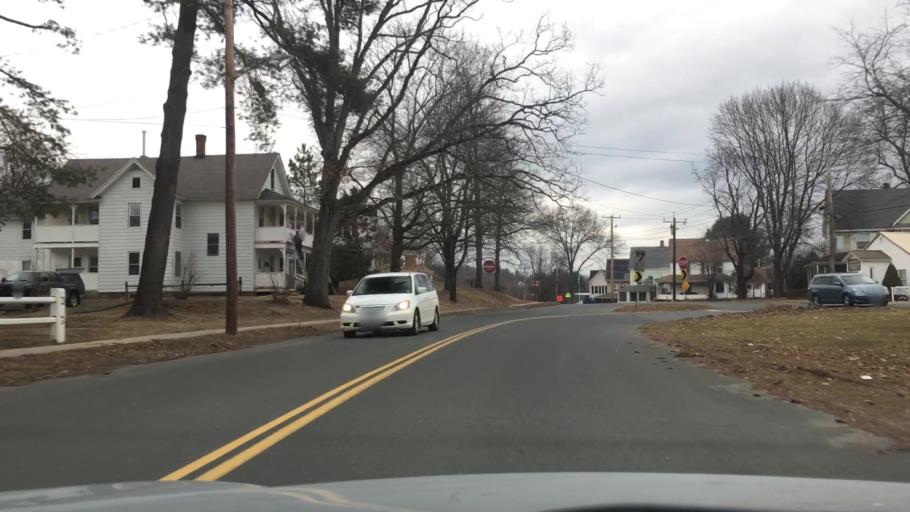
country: US
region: Massachusetts
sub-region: Franklin County
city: Greenfield
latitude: 42.6032
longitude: -72.6113
